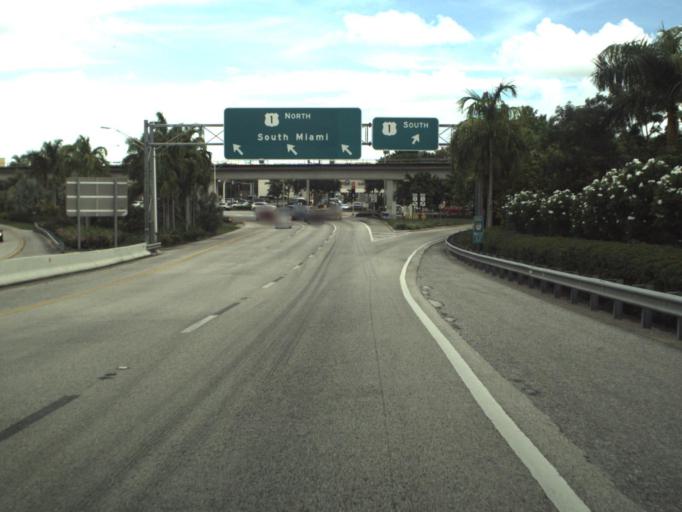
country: US
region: Florida
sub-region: Miami-Dade County
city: South Miami
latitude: 25.6939
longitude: -80.3047
